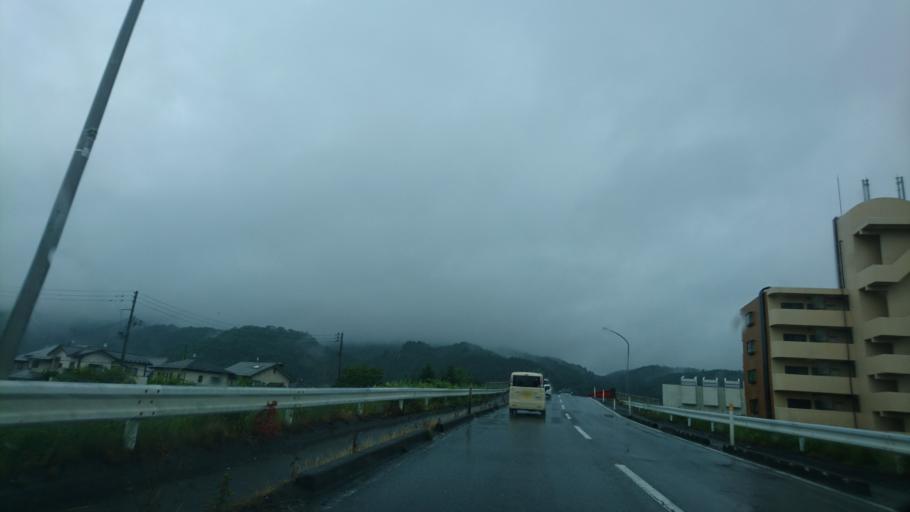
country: JP
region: Miyagi
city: Ishinomaki
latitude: 38.4404
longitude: 141.3137
